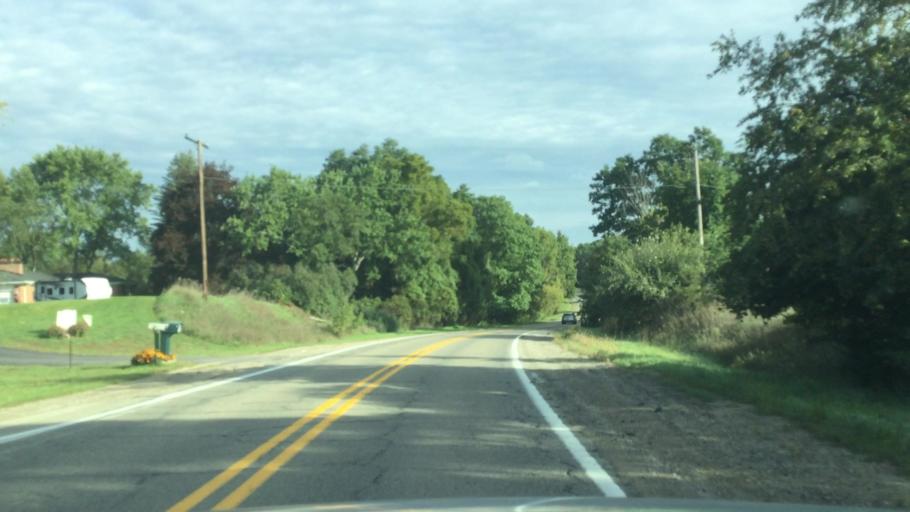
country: US
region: Michigan
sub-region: Livingston County
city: Brighton
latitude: 42.4965
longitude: -83.8596
